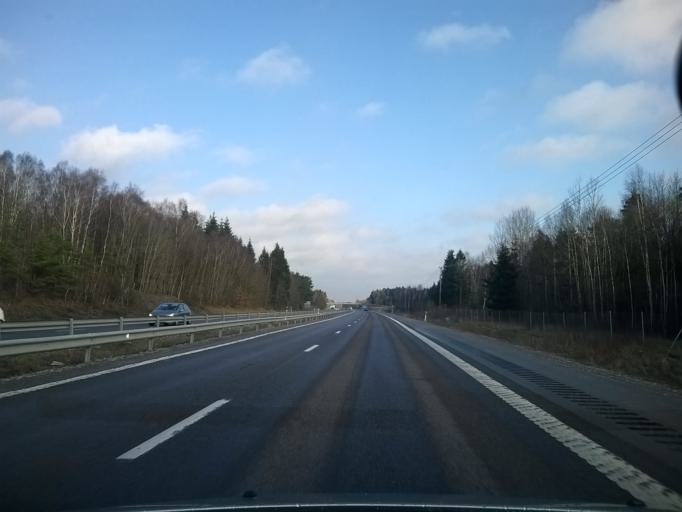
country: SE
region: Vaestra Goetaland
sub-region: Kungalvs Kommun
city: Kode
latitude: 57.9564
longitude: 11.8490
